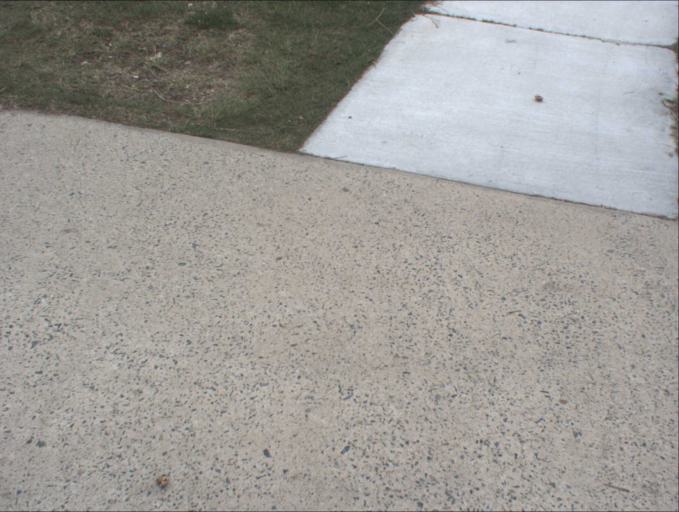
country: AU
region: Queensland
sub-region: Logan
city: Park Ridge South
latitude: -27.6959
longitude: 153.0251
